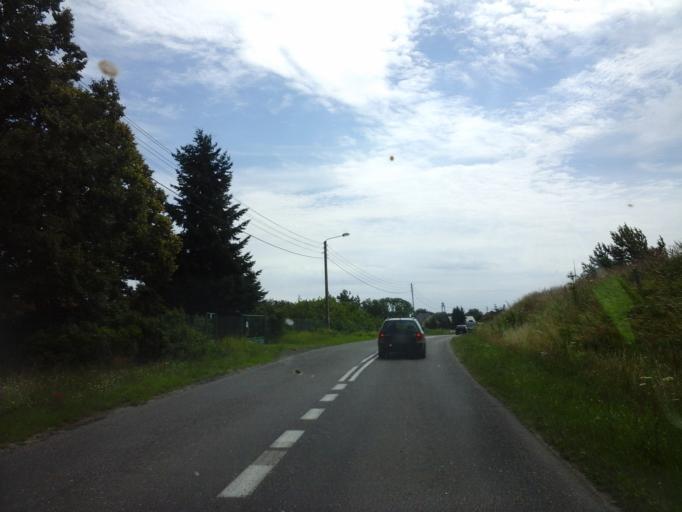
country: PL
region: West Pomeranian Voivodeship
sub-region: Powiat choszczenski
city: Bierzwnik
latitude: 53.0209
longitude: 15.7003
